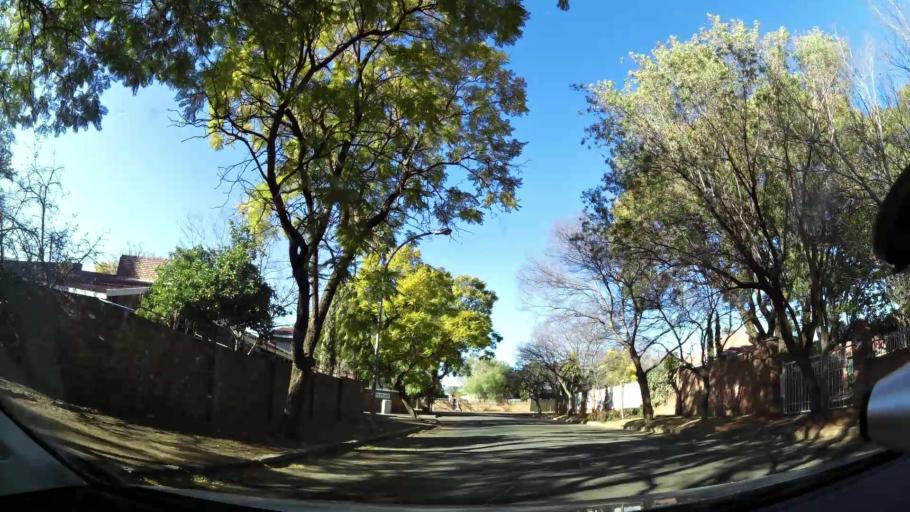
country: ZA
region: Northern Cape
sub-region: Frances Baard District Municipality
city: Kimberley
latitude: -28.7460
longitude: 24.7766
